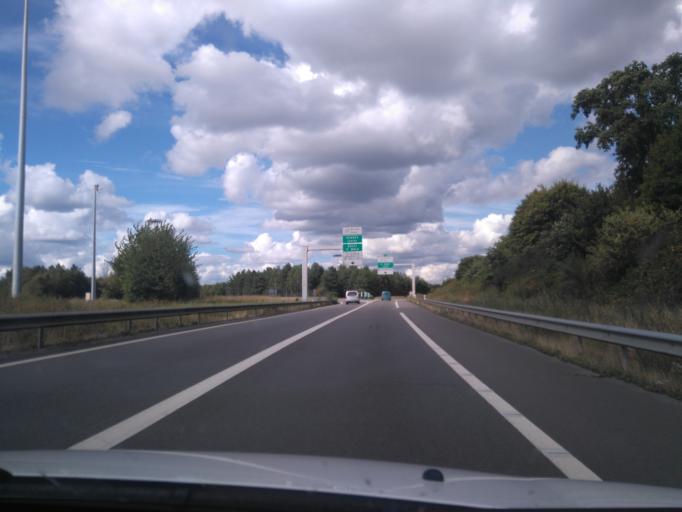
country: FR
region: Brittany
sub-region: Departement d'Ille-et-Vilaine
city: Rennes
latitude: 48.0776
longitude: -1.6748
